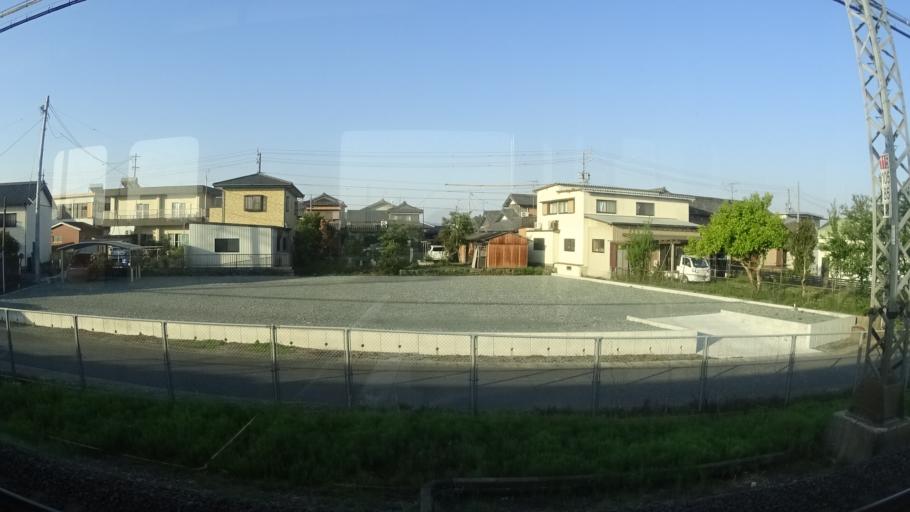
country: JP
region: Mie
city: Ise
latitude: 34.5414
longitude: 136.6001
